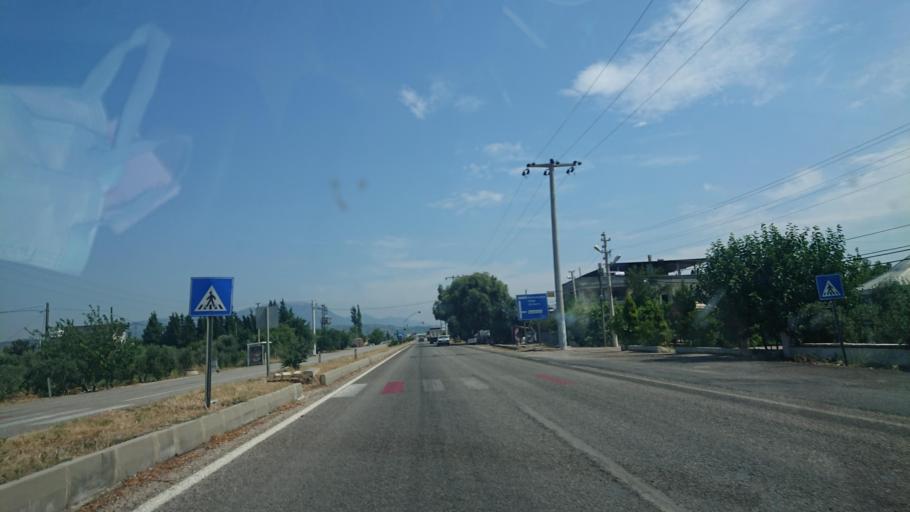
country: TR
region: Izmir
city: Torbali
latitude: 38.2124
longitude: 27.3684
